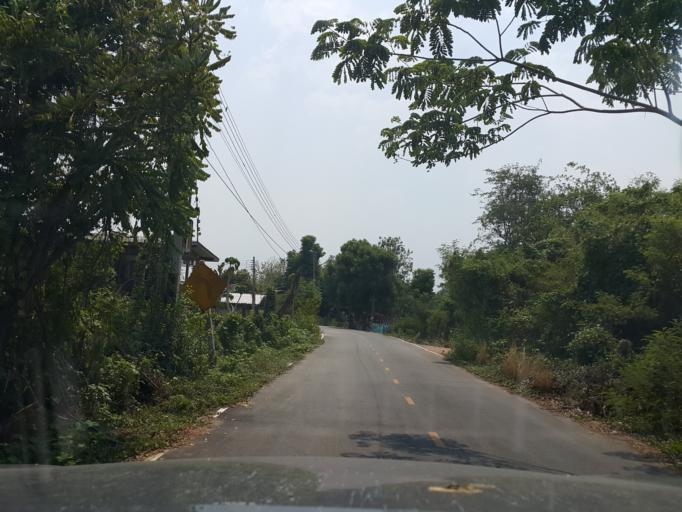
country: TH
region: Lampang
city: Mae Phrik
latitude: 17.5147
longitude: 99.1449
